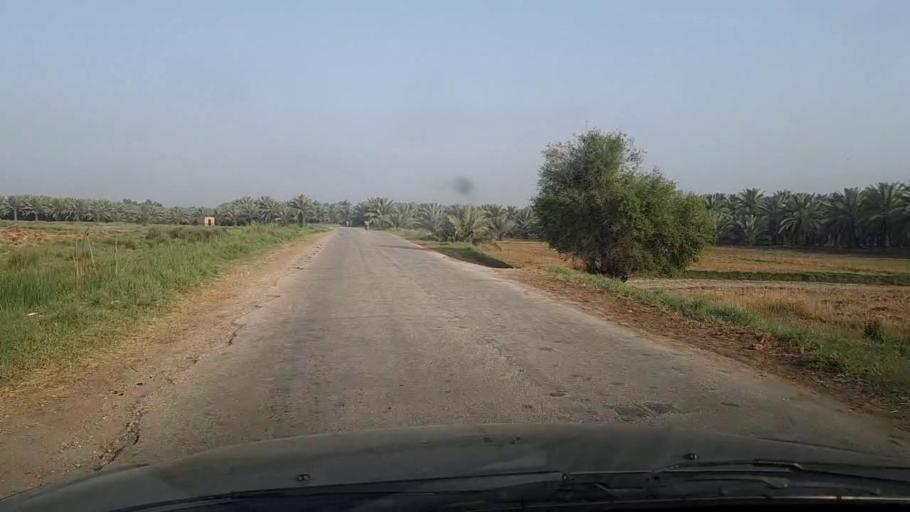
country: PK
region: Sindh
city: Khairpur
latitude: 27.5523
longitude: 68.6881
